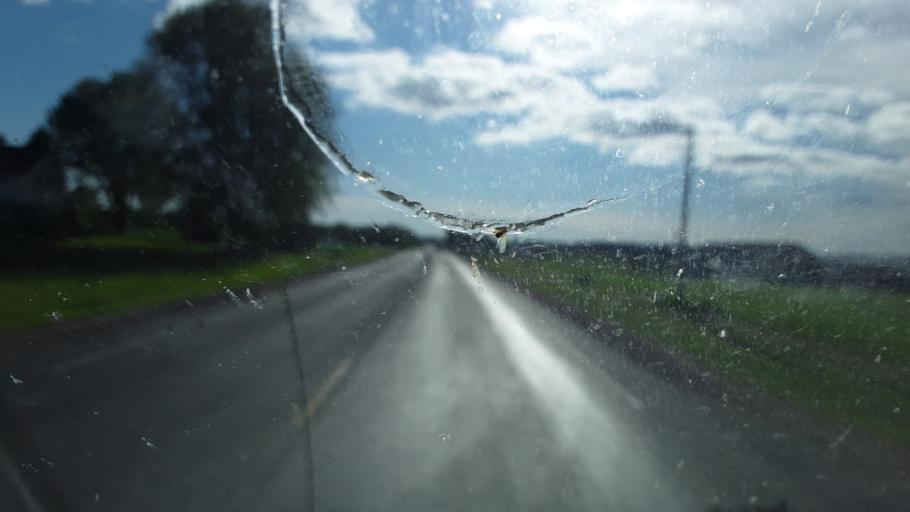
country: US
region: Wisconsin
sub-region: Marathon County
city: Spencer
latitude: 44.6562
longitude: -90.3368
